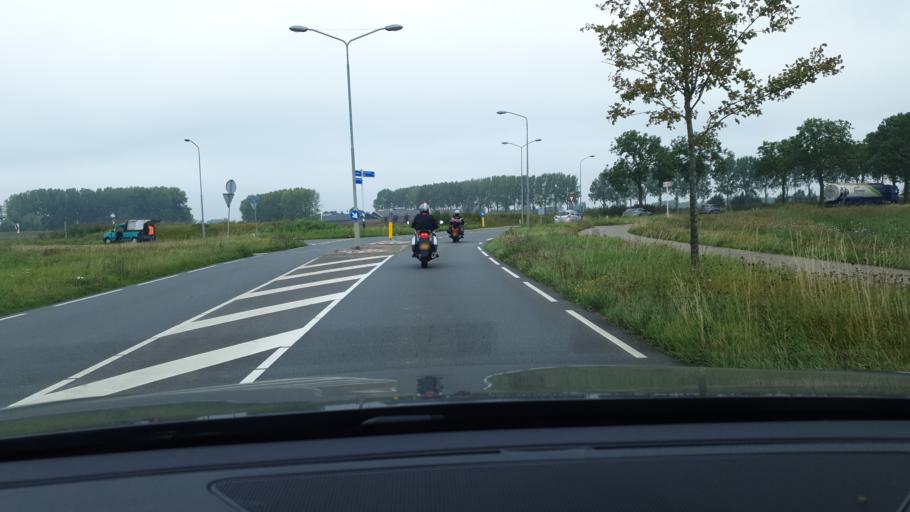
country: NL
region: North Brabant
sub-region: Gemeente 's-Hertogenbosch
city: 's-Hertogenbosch
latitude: 51.7387
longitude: 5.3448
